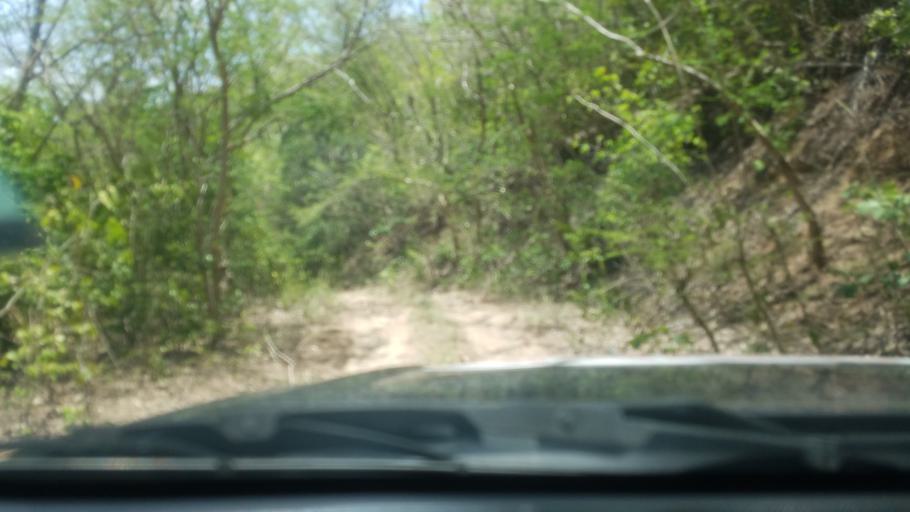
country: LC
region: Vieux-Fort
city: Vieux Fort
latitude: 13.7131
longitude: -60.9551
